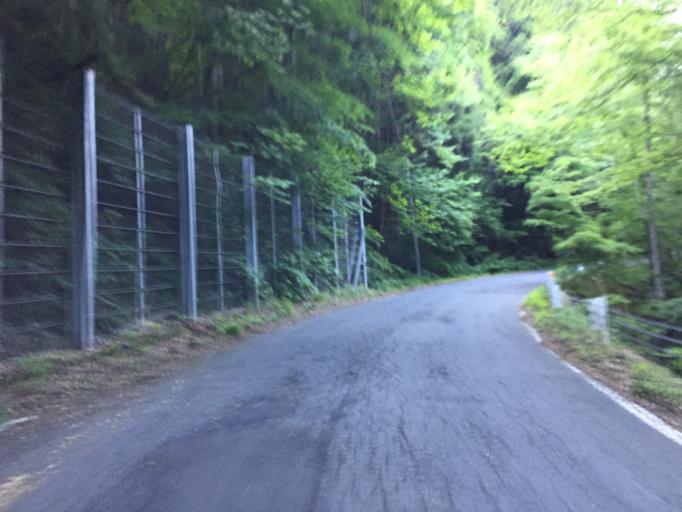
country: JP
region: Ibaraki
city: Kitaibaraki
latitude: 36.8854
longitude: 140.6270
